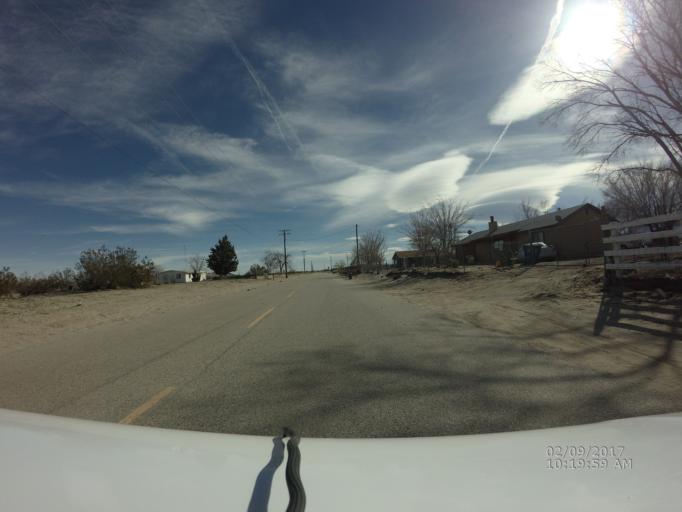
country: US
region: California
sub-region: Los Angeles County
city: Littlerock
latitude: 34.5725
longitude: -117.9186
